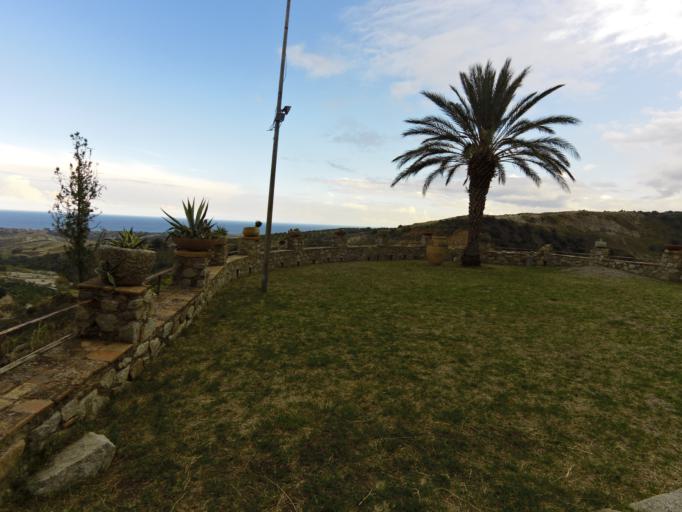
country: IT
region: Calabria
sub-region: Provincia di Catanzaro
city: Badolato
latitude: 38.5672
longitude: 16.5300
